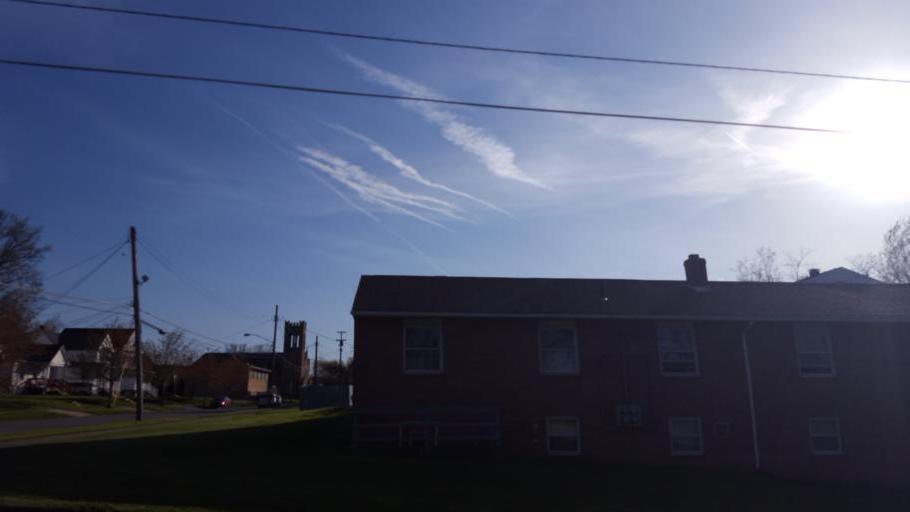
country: US
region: Ohio
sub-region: Ashtabula County
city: Ashtabula
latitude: 41.8974
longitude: -80.8017
